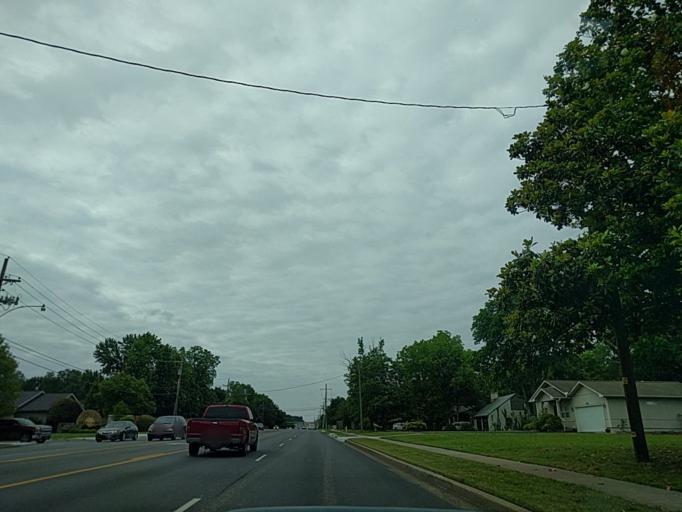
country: US
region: Oklahoma
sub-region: Tulsa County
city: Jenks
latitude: 36.0849
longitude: -95.9045
